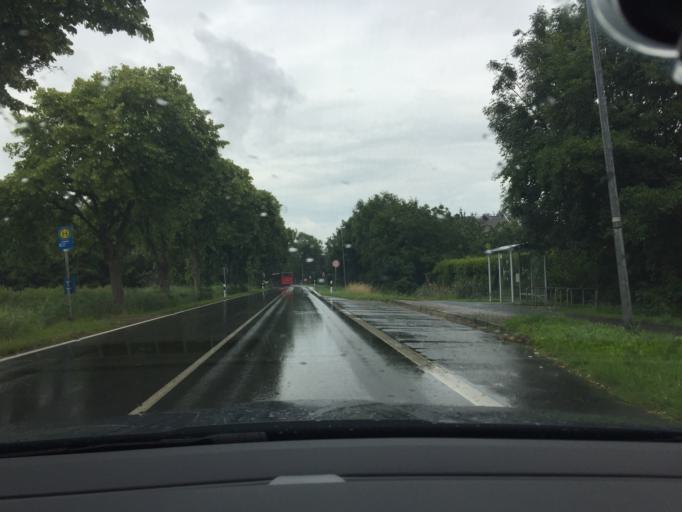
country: DE
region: Lower Saxony
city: Hinte
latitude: 53.4331
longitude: 7.0844
